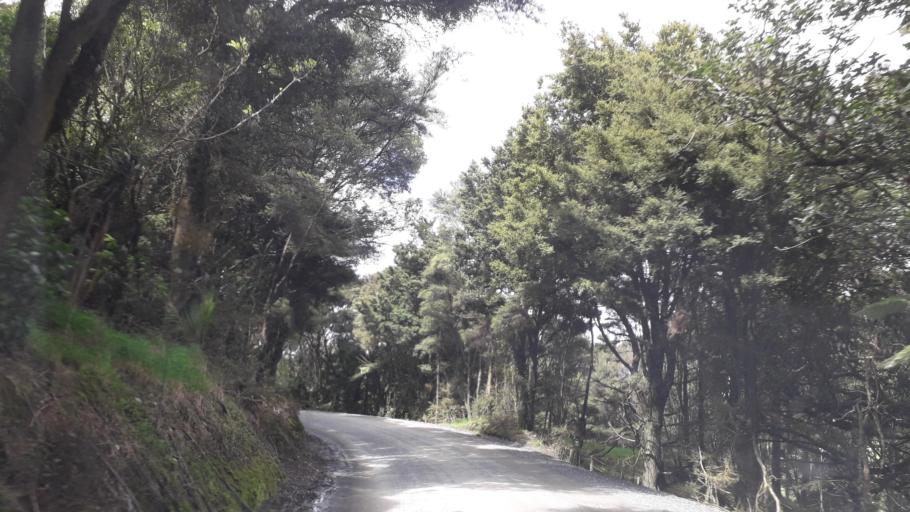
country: NZ
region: Northland
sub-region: Far North District
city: Kaitaia
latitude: -35.1705
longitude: 173.3394
